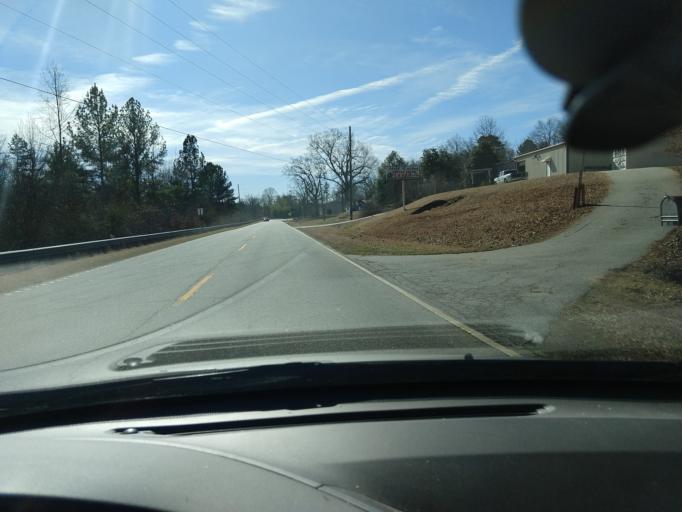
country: US
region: South Carolina
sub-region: Oconee County
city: Westminster
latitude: 34.6131
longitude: -83.1445
